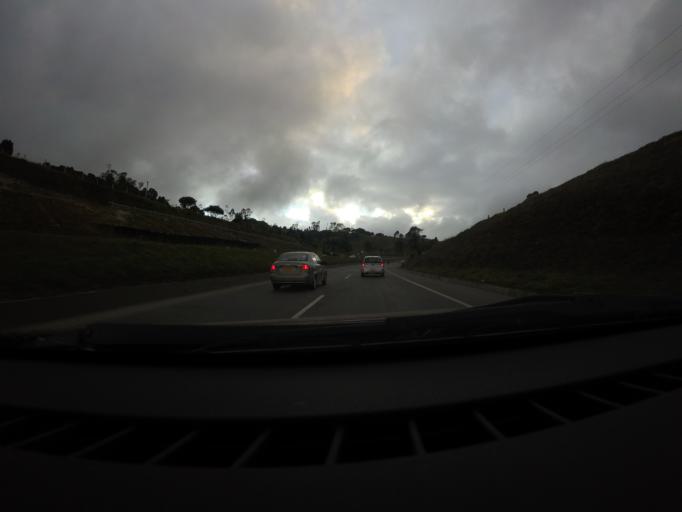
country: CO
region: Boyaca
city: Samaca
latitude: 5.4389
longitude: -73.4428
